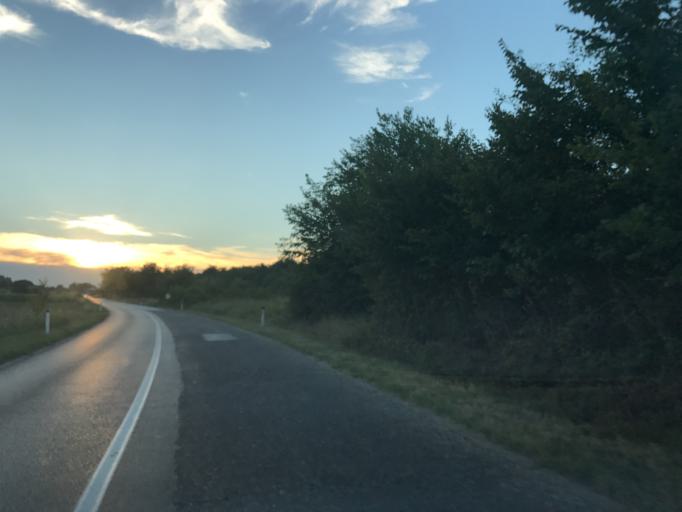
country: RS
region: Central Serbia
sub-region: Branicevski Okrug
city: Golubac
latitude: 44.6863
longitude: 21.5828
